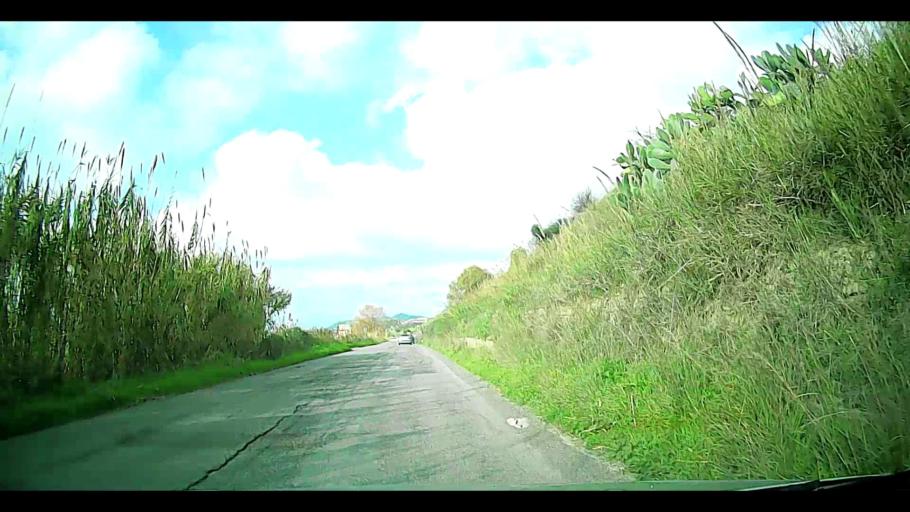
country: IT
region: Calabria
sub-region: Provincia di Crotone
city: Rocca di Neto
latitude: 39.1800
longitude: 17.0300
